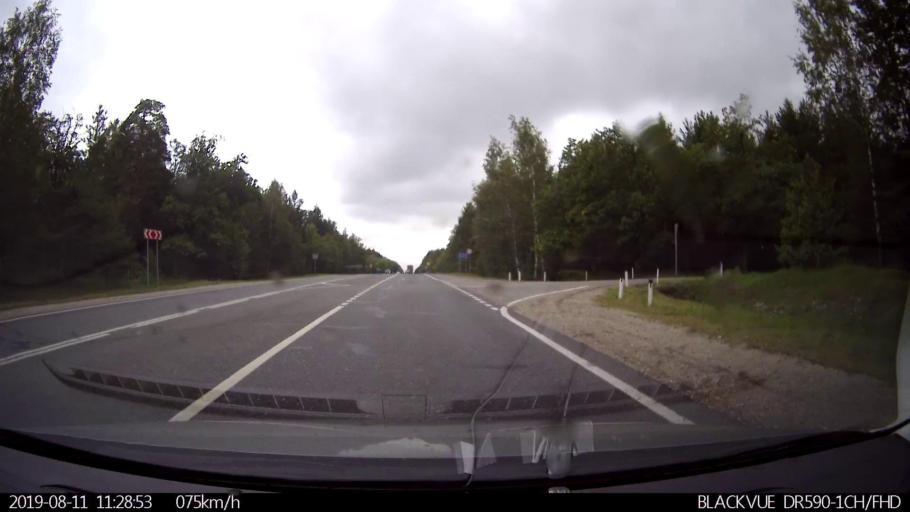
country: RU
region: Ulyanovsk
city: Krasnyy Gulyay
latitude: 54.0763
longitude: 48.2261
